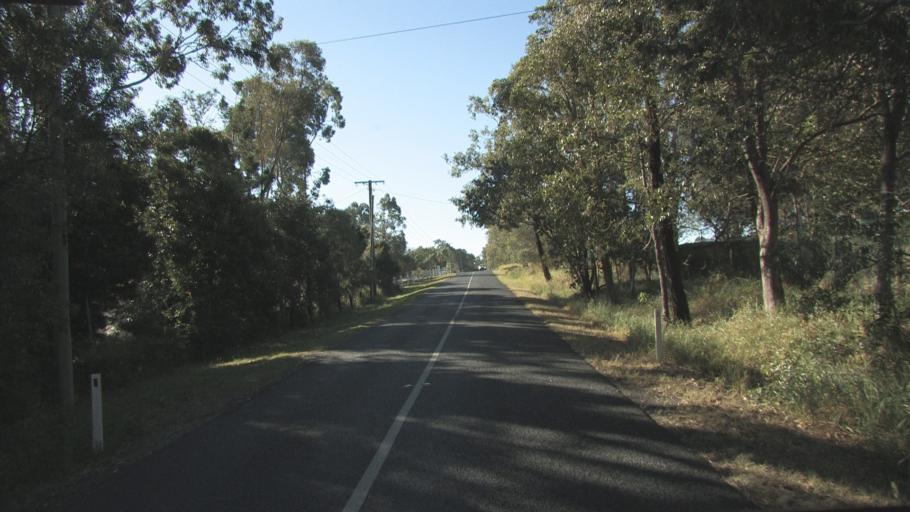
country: AU
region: Queensland
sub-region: Logan
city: Logan Reserve
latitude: -27.7326
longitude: 153.1041
